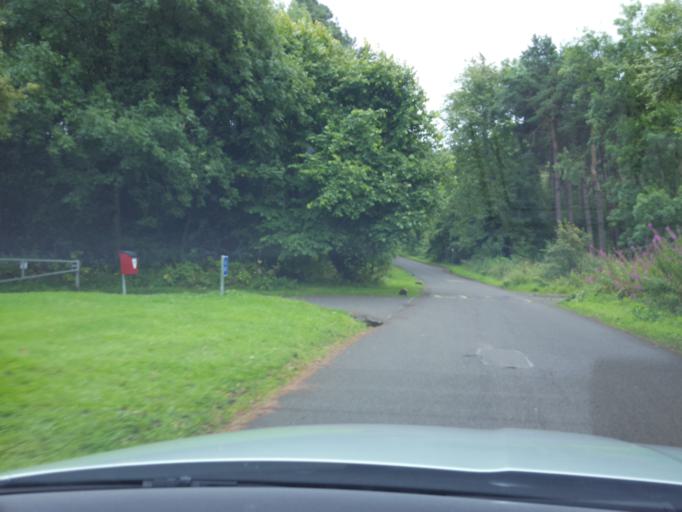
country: GB
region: Scotland
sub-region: Falkirk
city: Polmont
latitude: 55.9628
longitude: -3.6675
